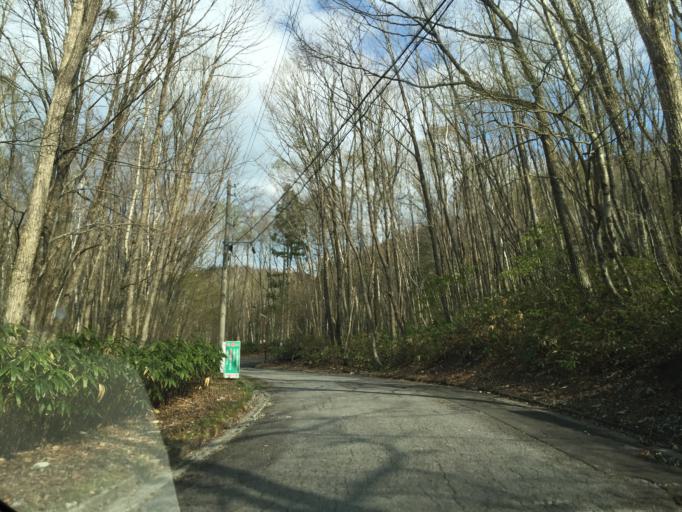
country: JP
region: Nagano
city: Iida
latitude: 35.3526
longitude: 137.6776
